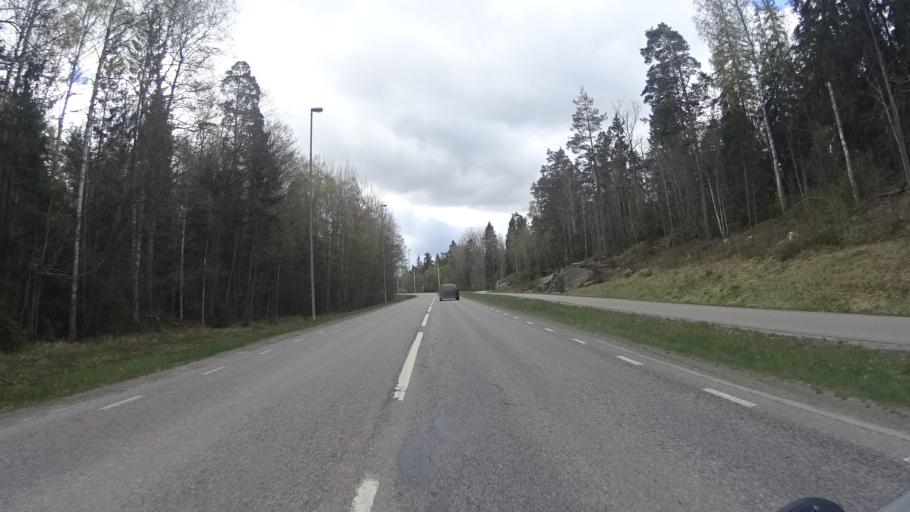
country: SE
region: Stockholm
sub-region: Botkyrka Kommun
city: Tullinge
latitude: 59.2039
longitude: 17.9249
